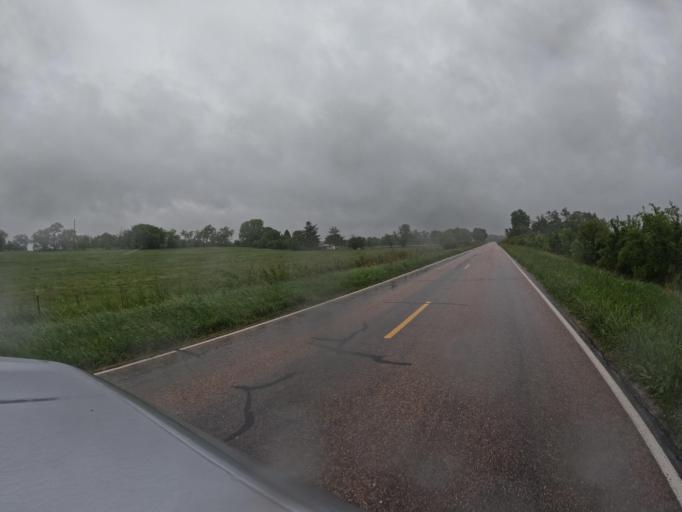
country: US
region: Nebraska
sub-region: Gage County
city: Wymore
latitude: 40.1258
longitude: -96.6526
